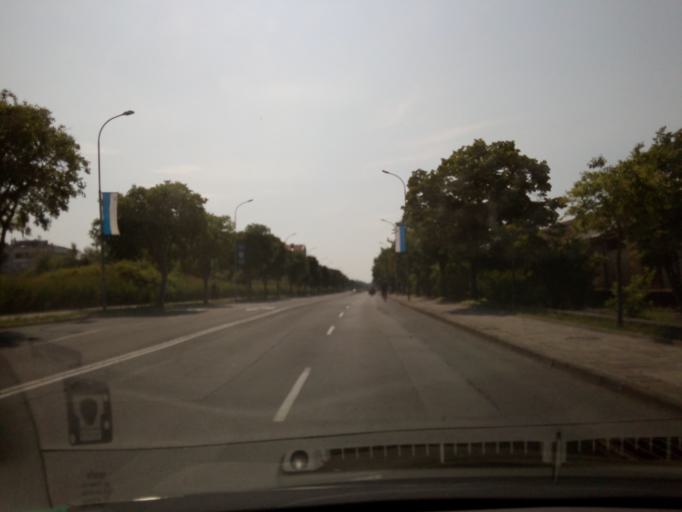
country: BG
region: Burgas
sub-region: Obshtina Pomorie
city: Pomorie
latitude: 42.5647
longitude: 27.6248
